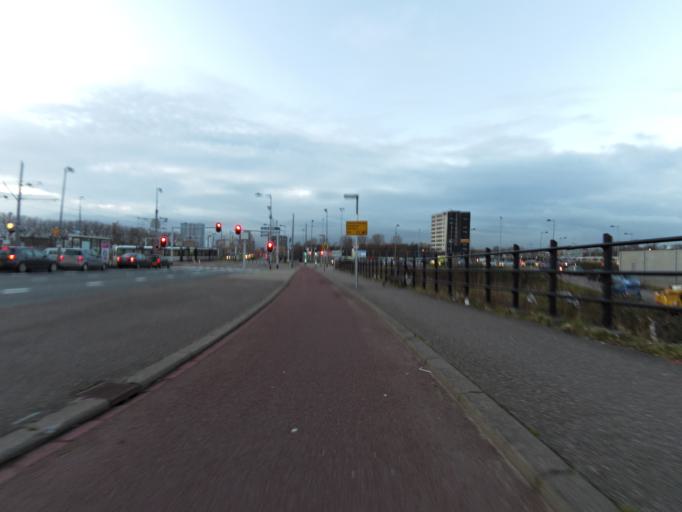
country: NL
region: South Holland
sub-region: Gemeente Rotterdam
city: Rotterdam
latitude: 51.9004
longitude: 4.5124
